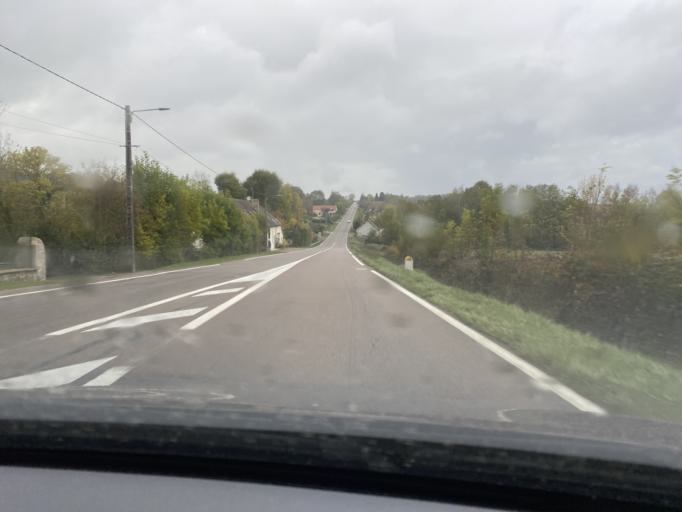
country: FR
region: Bourgogne
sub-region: Departement de la Cote-d'Or
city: Saulieu
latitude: 47.2896
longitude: 4.2220
